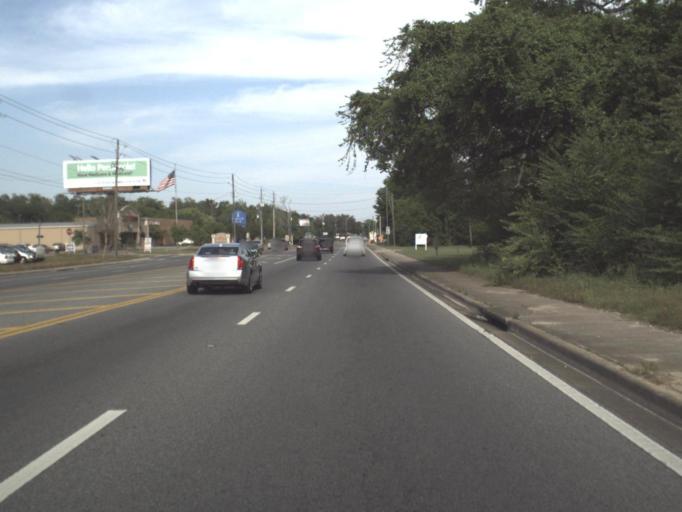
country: US
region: Florida
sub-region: Escambia County
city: Ferry Pass
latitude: 30.4961
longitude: -87.2208
